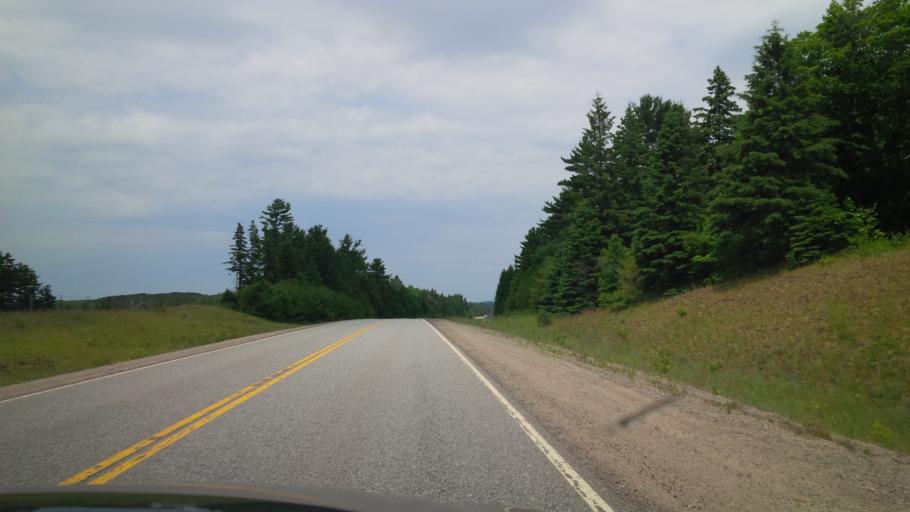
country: CA
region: Ontario
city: Huntsville
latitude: 45.5178
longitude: -79.3115
